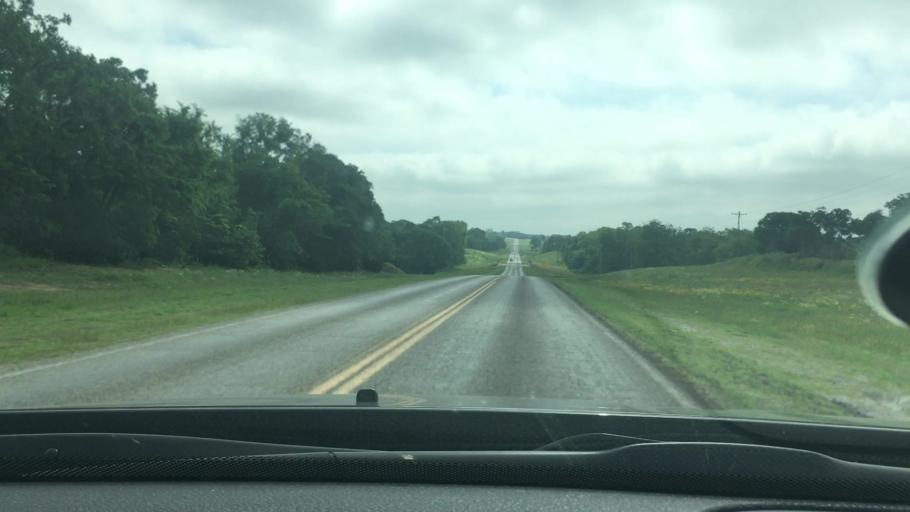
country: US
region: Oklahoma
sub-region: Johnston County
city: Tishomingo
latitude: 34.2303
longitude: -96.6498
